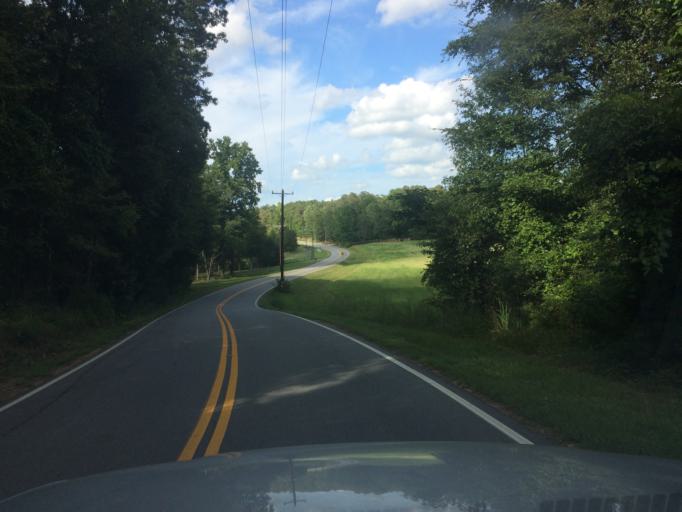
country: US
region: South Carolina
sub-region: Spartanburg County
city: Woodruff
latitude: 34.7419
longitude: -82.1126
